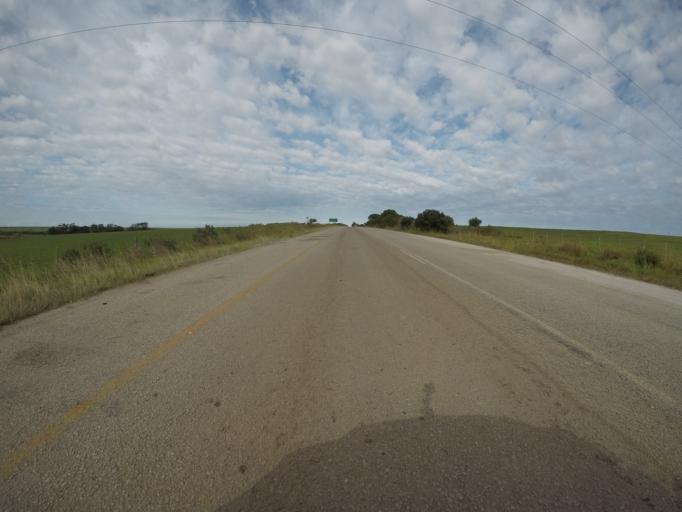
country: ZA
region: Eastern Cape
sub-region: Cacadu District Municipality
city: Kareedouw
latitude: -34.0470
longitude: 24.4578
